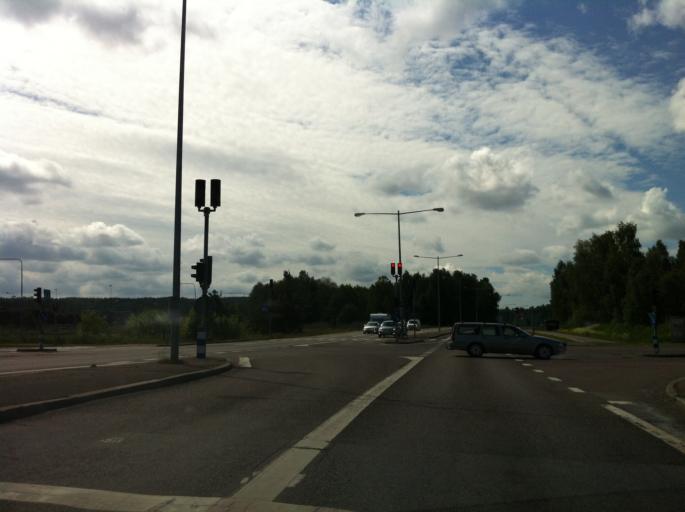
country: SE
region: Vaermland
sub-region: Grums Kommun
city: Grums
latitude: 59.3410
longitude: 13.1095
